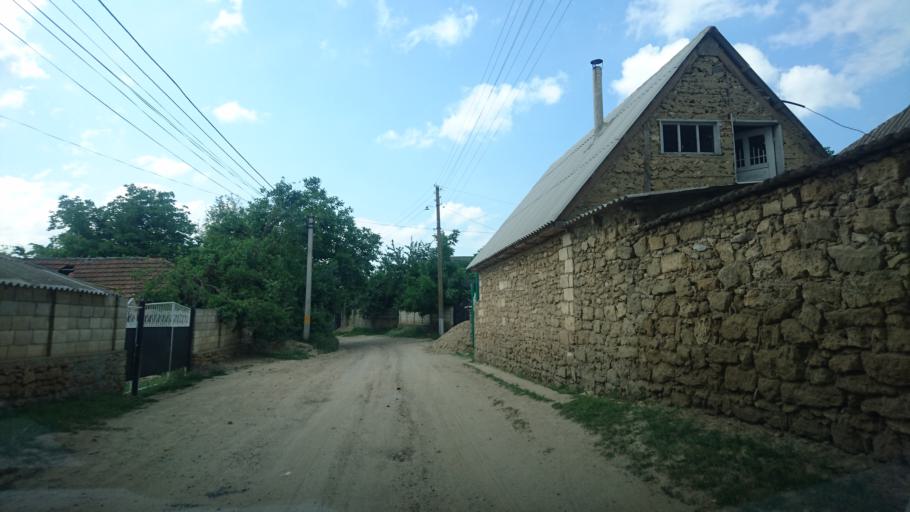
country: MD
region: Telenesti
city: Cocieri
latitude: 47.3599
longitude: 29.1034
